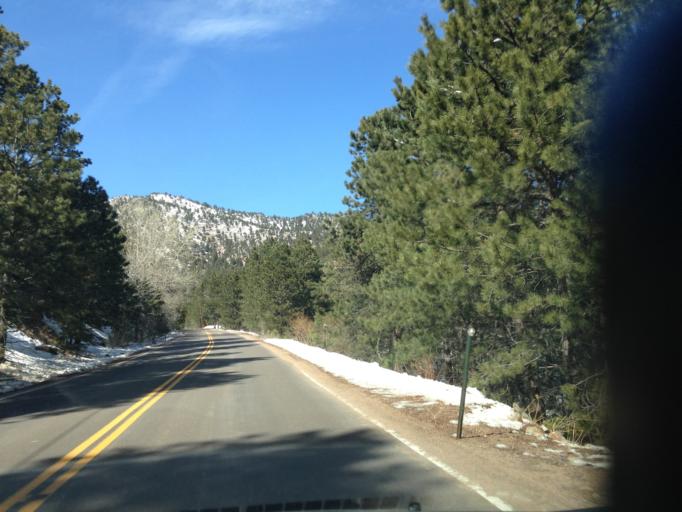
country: US
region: Colorado
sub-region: Boulder County
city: Lyons
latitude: 40.1242
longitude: -105.3982
